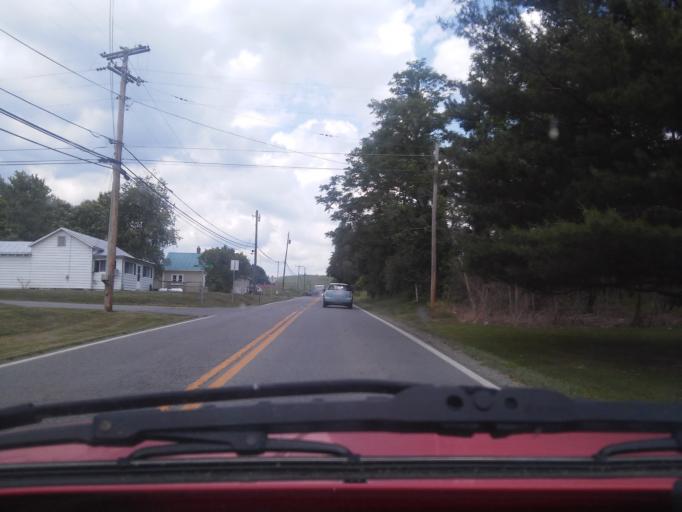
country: US
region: Virginia
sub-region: Craig County
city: New Castle
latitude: 37.5070
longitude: -80.1055
